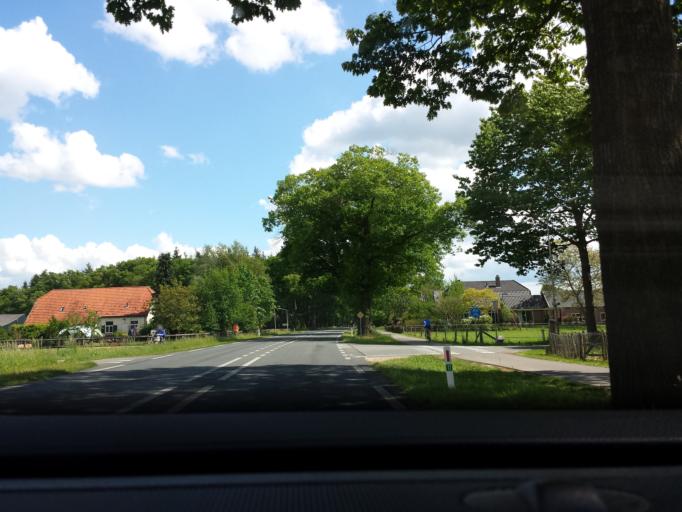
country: NL
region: Gelderland
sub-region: Gemeente Lochem
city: Almen
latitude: 52.1206
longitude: 6.2898
